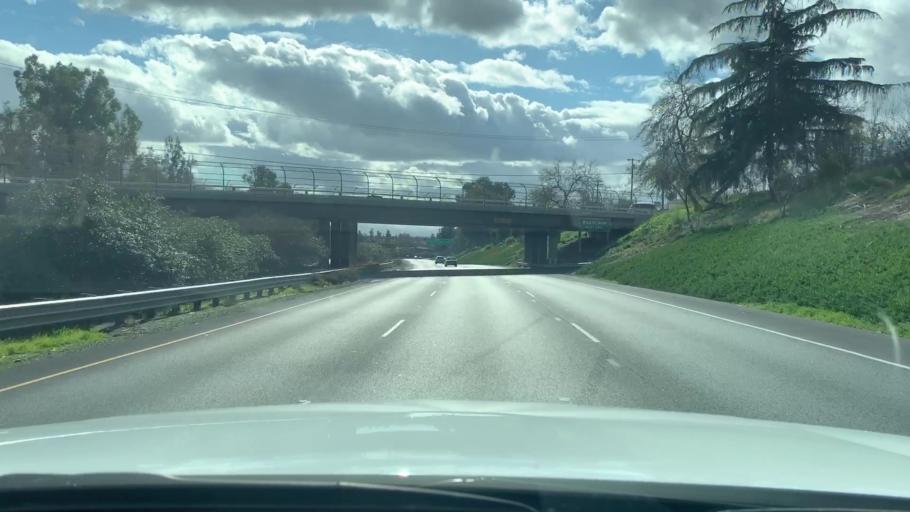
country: US
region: California
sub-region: Kern County
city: Bakersfield
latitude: 35.3903
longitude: -118.9805
